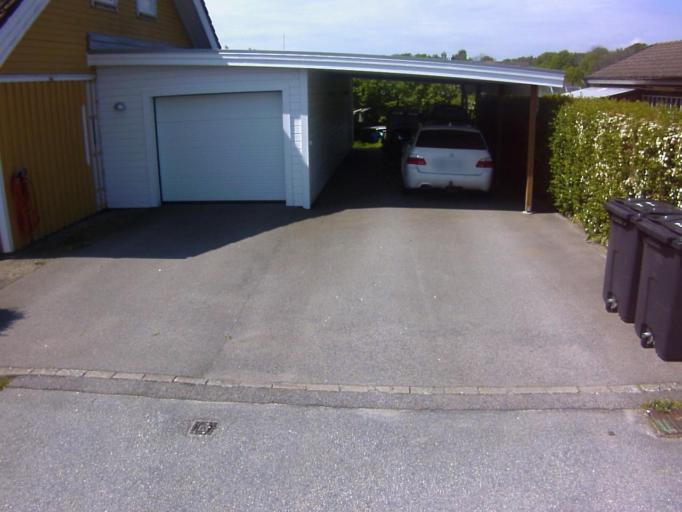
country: SE
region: Blekinge
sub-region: Solvesborgs Kommun
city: Soelvesborg
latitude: 56.0434
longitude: 14.5686
